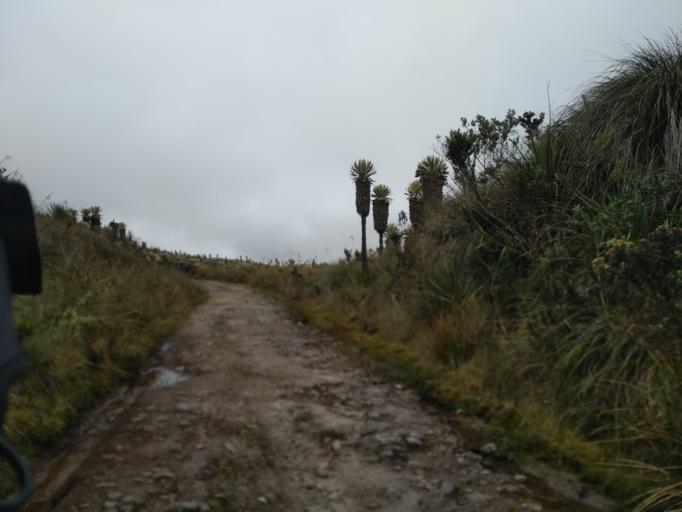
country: EC
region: Carchi
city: San Gabriel
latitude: 0.6852
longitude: -77.8547
